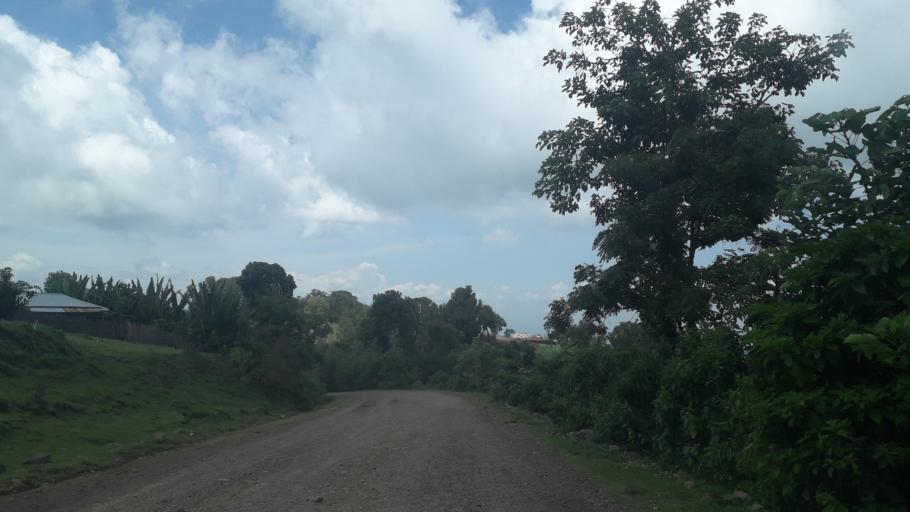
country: ET
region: Oromiya
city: Jima
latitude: 7.4507
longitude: 36.8735
